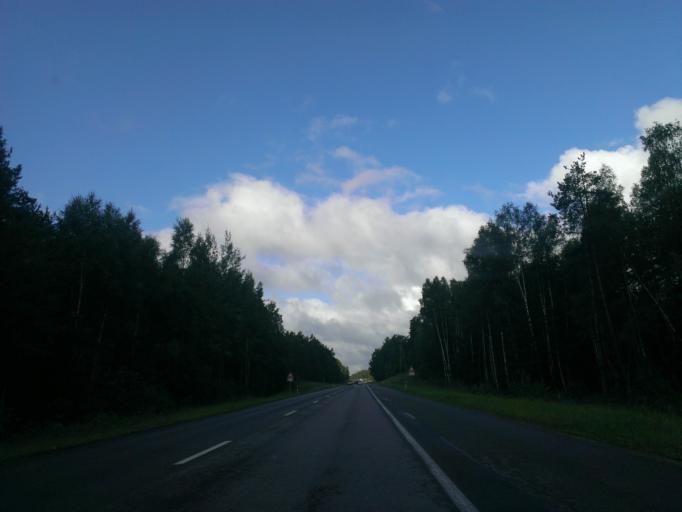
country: LV
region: Incukalns
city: Vangazi
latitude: 57.0850
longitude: 24.5361
